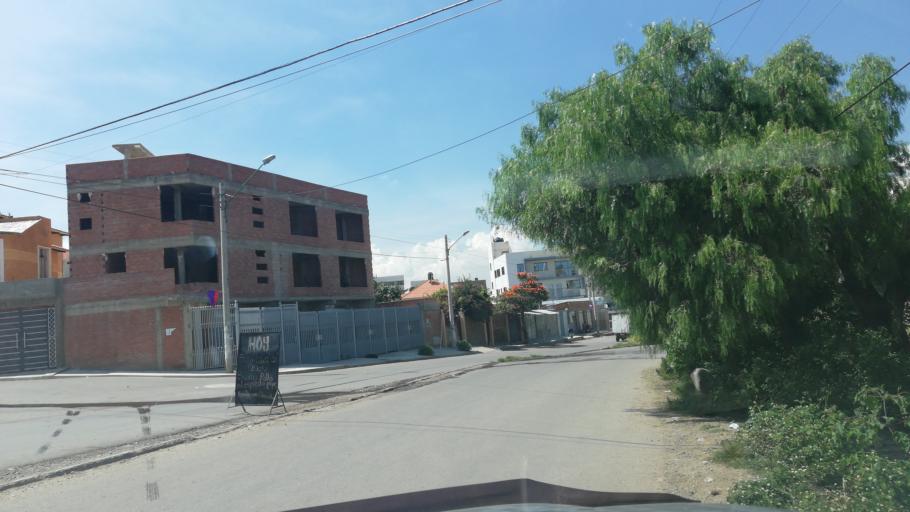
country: BO
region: Cochabamba
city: Cochabamba
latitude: -17.3474
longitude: -66.1767
